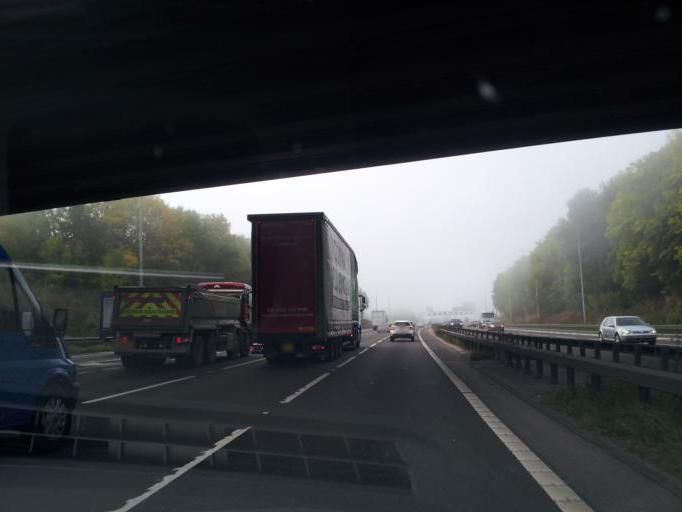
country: GB
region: England
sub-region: Kirklees
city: Cleckheaton
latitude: 53.7286
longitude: -1.7330
